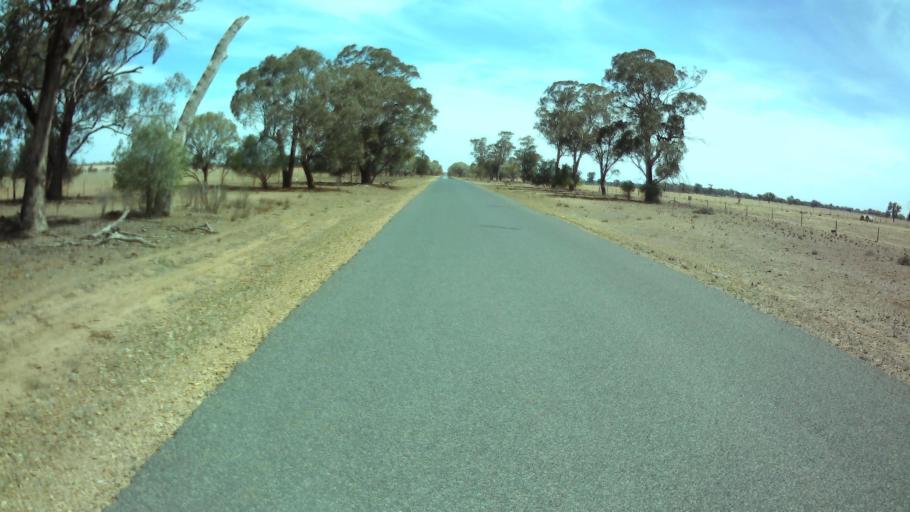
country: AU
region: New South Wales
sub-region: Weddin
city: Grenfell
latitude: -33.8670
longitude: 147.7454
